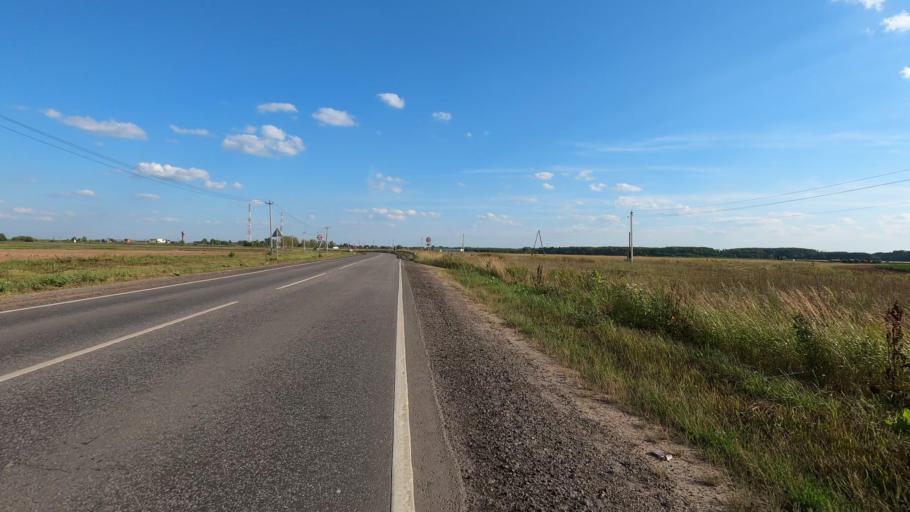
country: RU
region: Moskovskaya
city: Raduzhnyy
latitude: 55.1651
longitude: 38.7268
